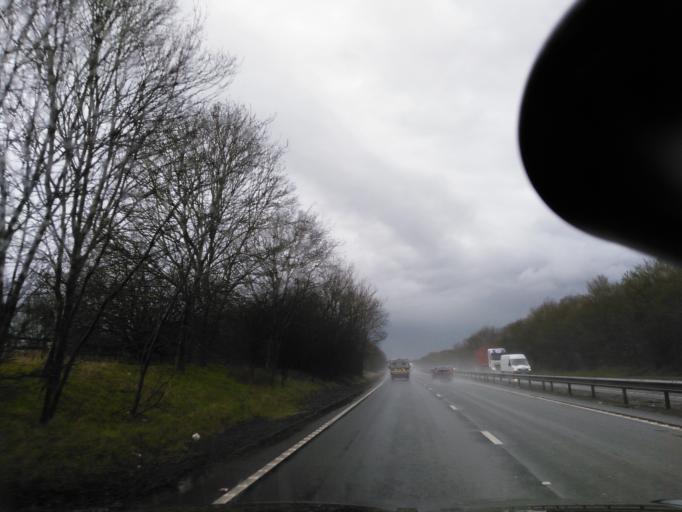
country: GB
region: England
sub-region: North Yorkshire
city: Thirsk
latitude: 54.2397
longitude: -1.3299
